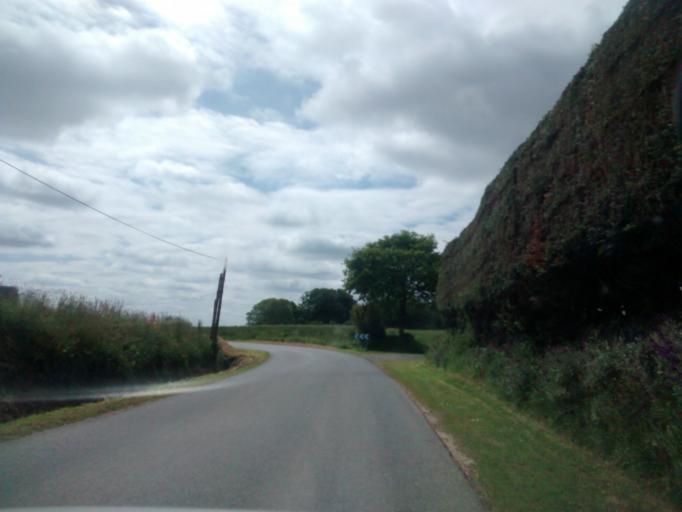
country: FR
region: Brittany
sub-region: Departement des Cotes-d'Armor
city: Langoat
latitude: 48.7704
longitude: -3.3020
